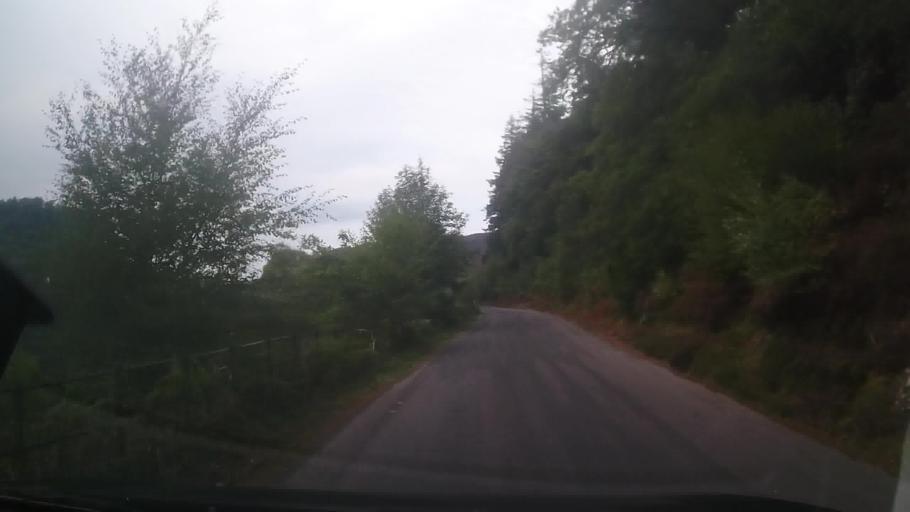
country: GB
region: Wales
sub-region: Sir Powys
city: Rhayader
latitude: 52.2652
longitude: -3.5972
